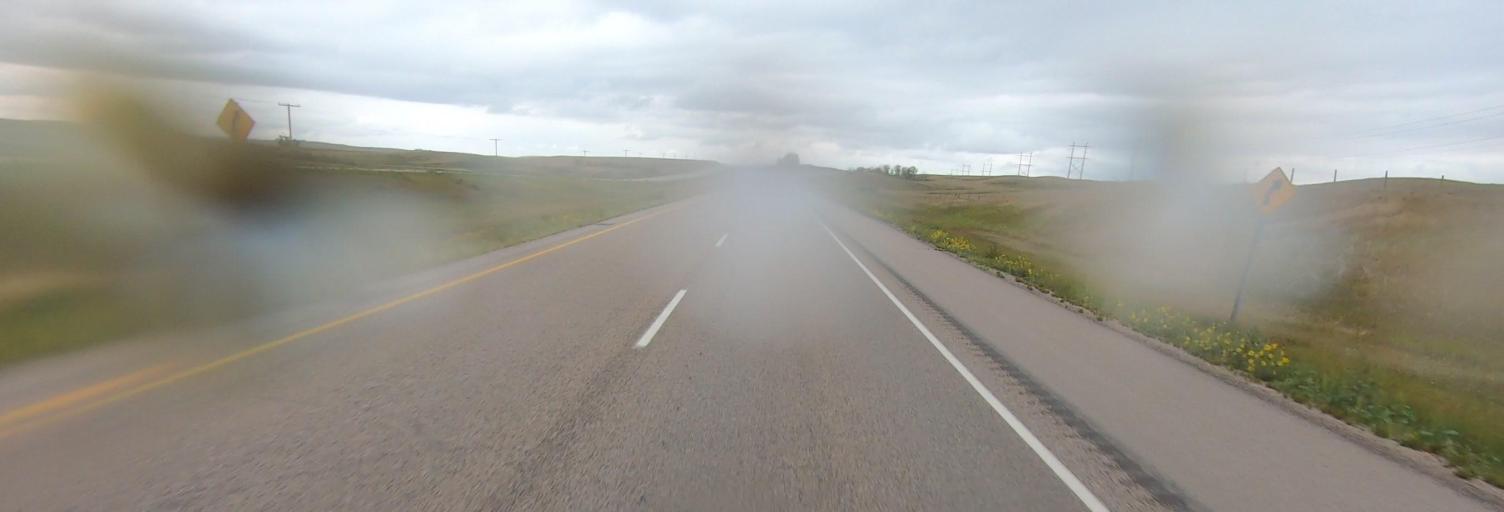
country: CA
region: Saskatchewan
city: Gravelbourg
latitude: 50.4630
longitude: -106.4328
